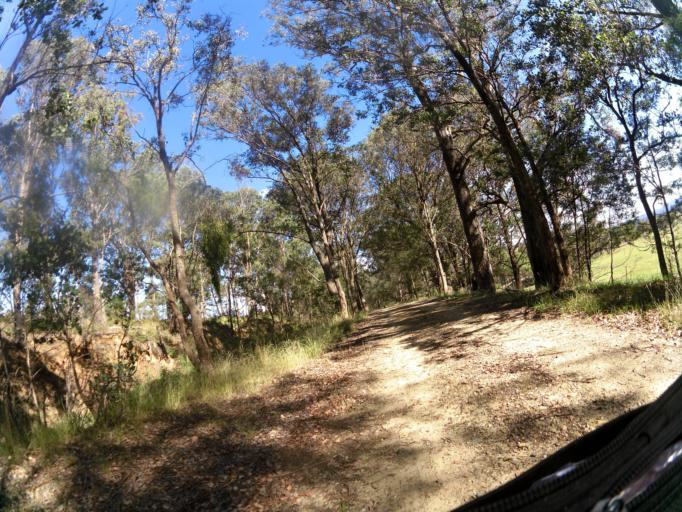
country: AU
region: Victoria
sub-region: East Gippsland
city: Lakes Entrance
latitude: -37.7347
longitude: 148.1640
